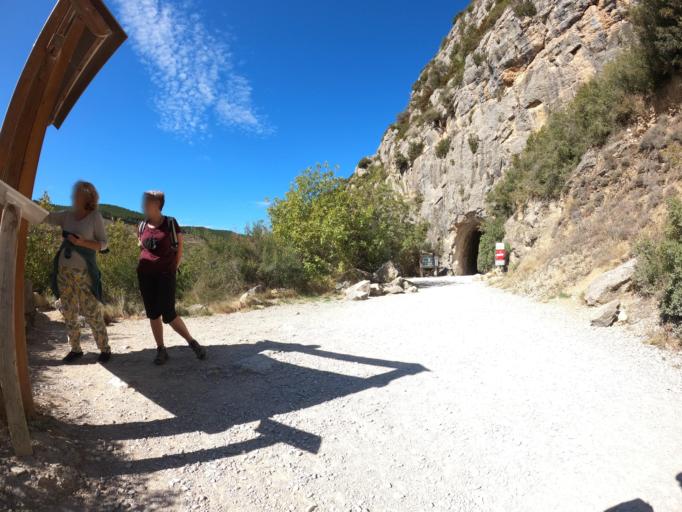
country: ES
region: Navarre
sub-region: Provincia de Navarra
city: Liedena
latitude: 42.6250
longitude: -1.3015
